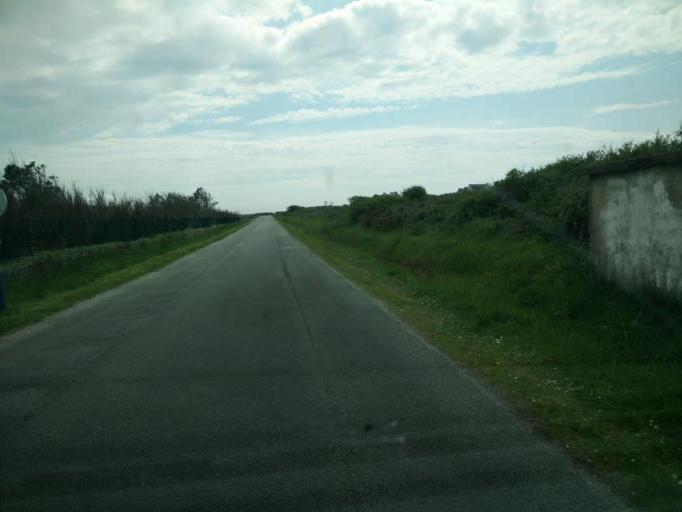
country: FR
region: Brittany
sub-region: Departement du Finistere
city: Camaret-sur-Mer
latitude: 48.2759
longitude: -4.6092
